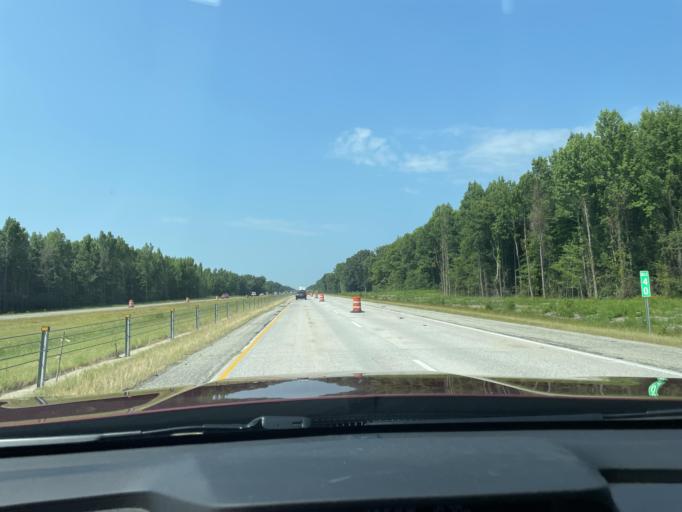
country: US
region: Arkansas
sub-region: White County
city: Searcy
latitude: 35.1824
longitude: -91.7569
